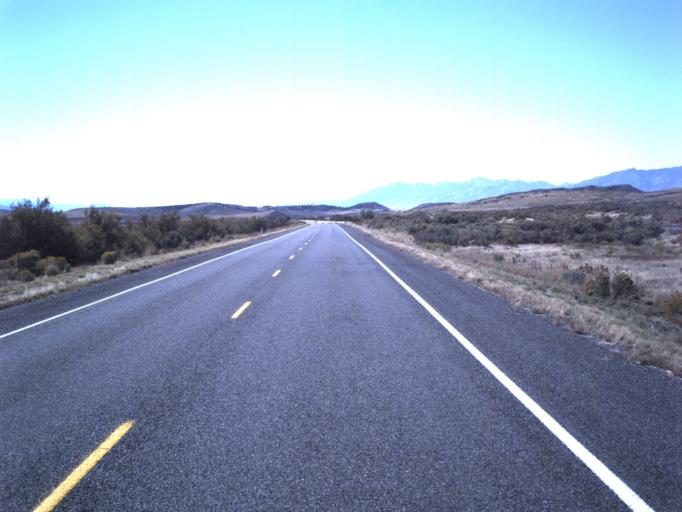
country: US
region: Utah
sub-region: Juab County
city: Nephi
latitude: 39.5001
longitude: -111.9586
